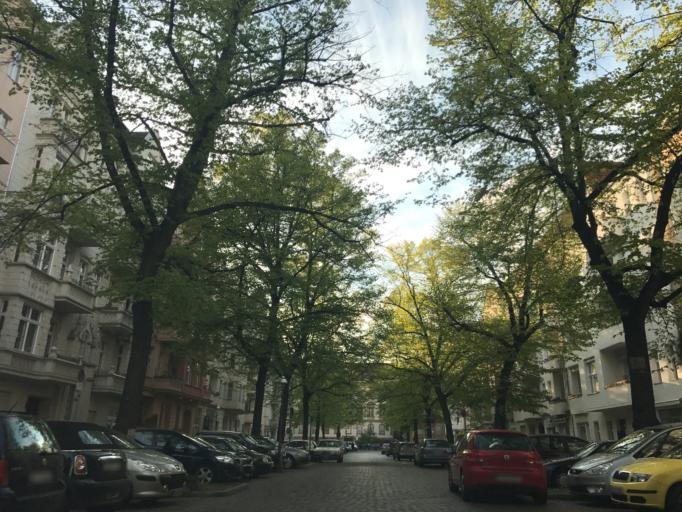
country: DE
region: Berlin
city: Halensee
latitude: 52.5052
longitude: 13.2973
